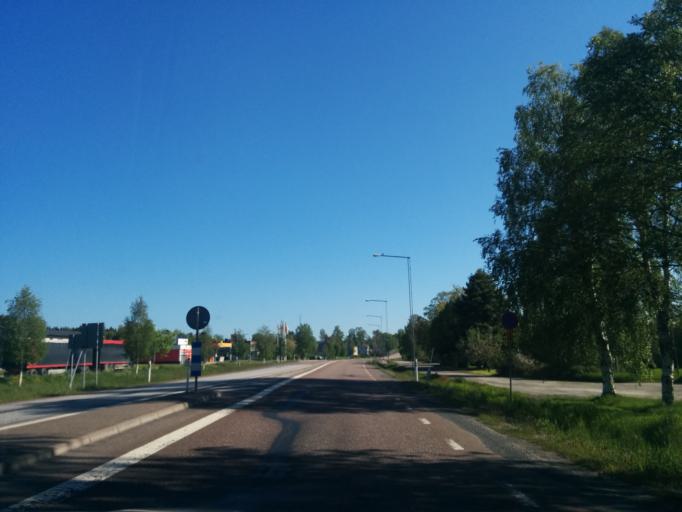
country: SE
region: Vaesternorrland
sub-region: Haernoesands Kommun
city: Haernoesand
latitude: 62.6741
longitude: 17.8408
